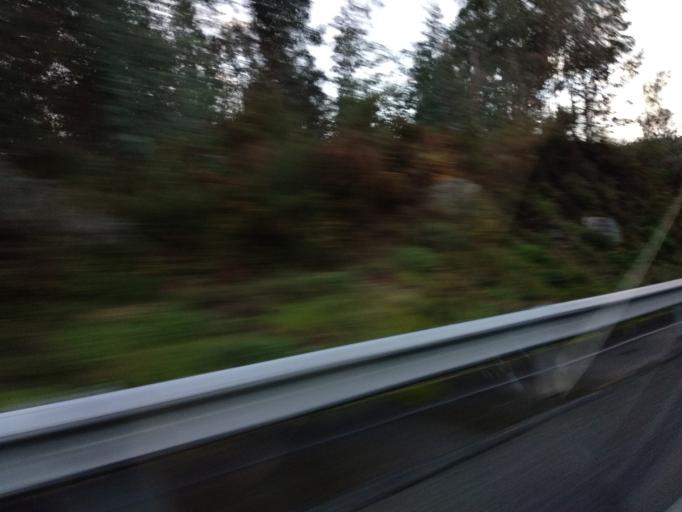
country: PT
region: Braga
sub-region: Braga
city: Oliveira
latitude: 41.4784
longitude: -8.4592
